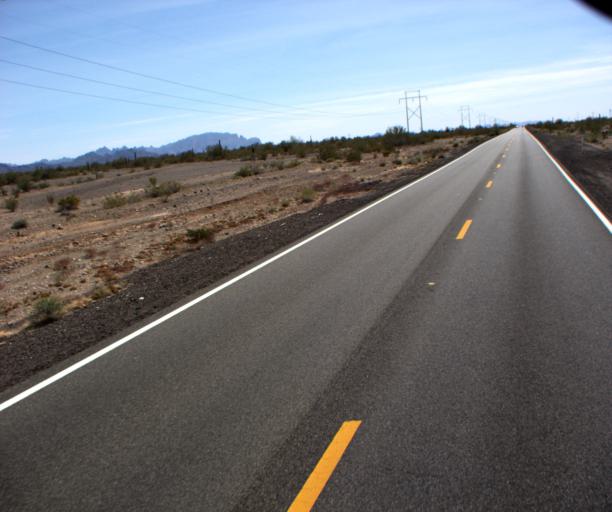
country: US
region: Arizona
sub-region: La Paz County
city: Quartzsite
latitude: 33.5689
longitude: -114.2171
